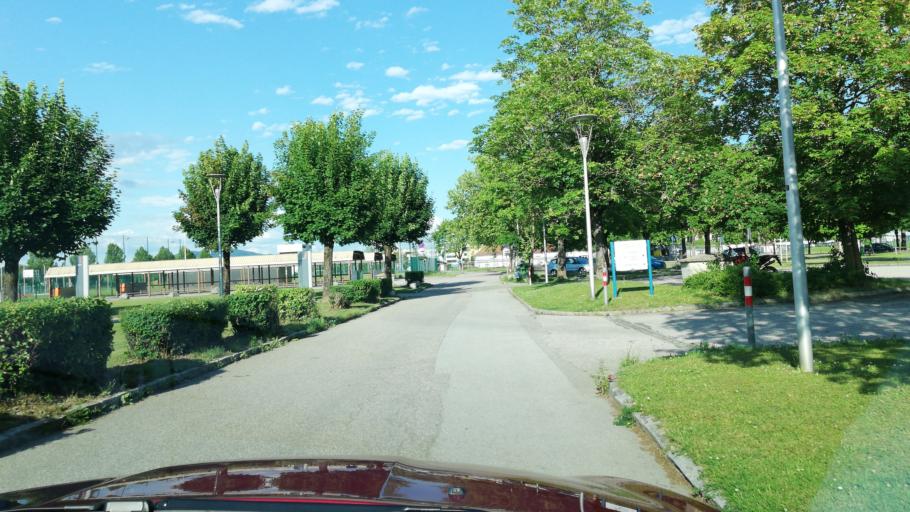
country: AT
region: Upper Austria
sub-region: Politischer Bezirk Linz-Land
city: Leonding
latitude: 48.2679
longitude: 14.2521
